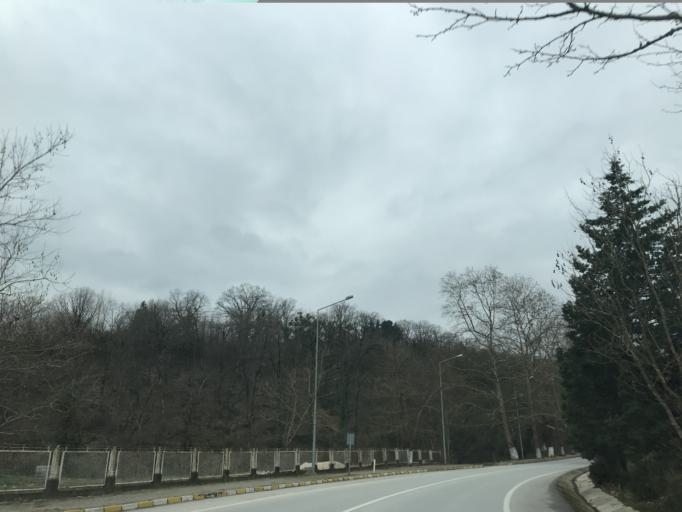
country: TR
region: Yalova
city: Termal
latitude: 40.6020
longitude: 29.1839
